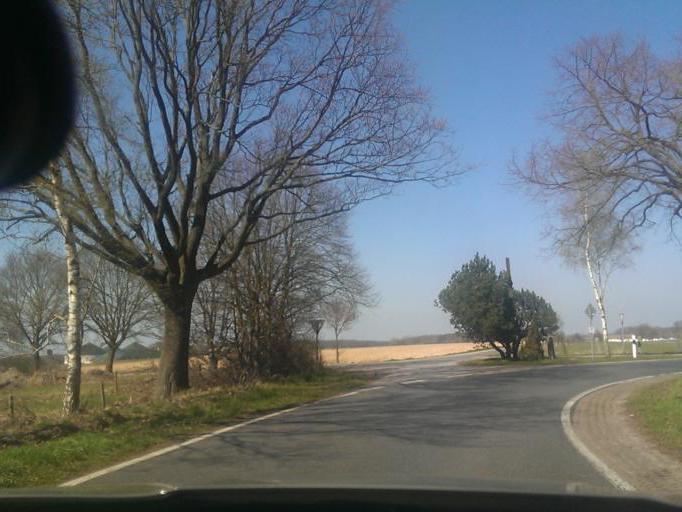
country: DE
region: Lower Saxony
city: Elze
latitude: 52.5423
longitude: 9.7197
